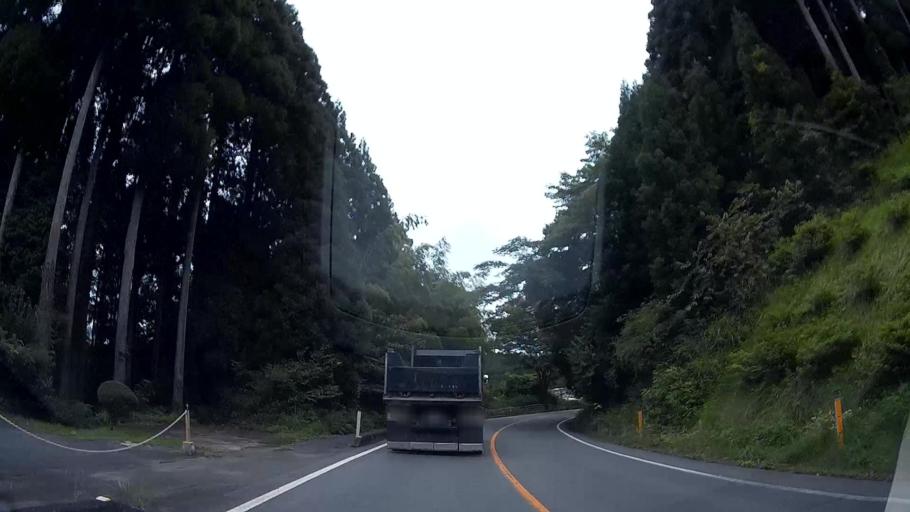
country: JP
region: Oita
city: Tsukawaki
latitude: 33.1265
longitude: 131.0593
